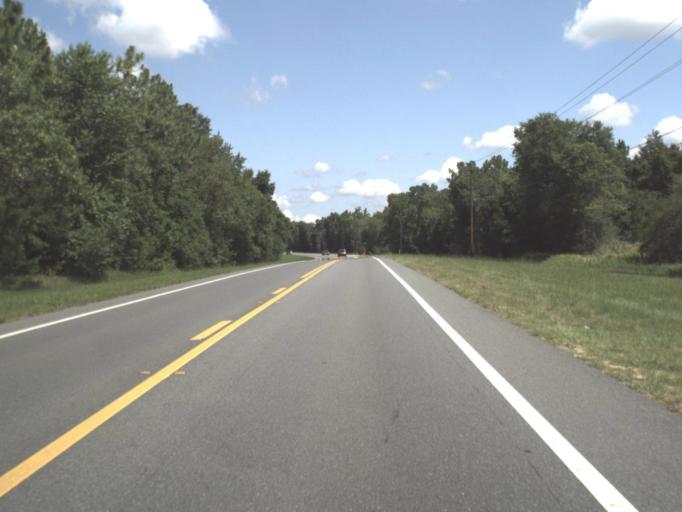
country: US
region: Florida
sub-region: Clay County
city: Keystone Heights
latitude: 29.7553
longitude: -81.9971
